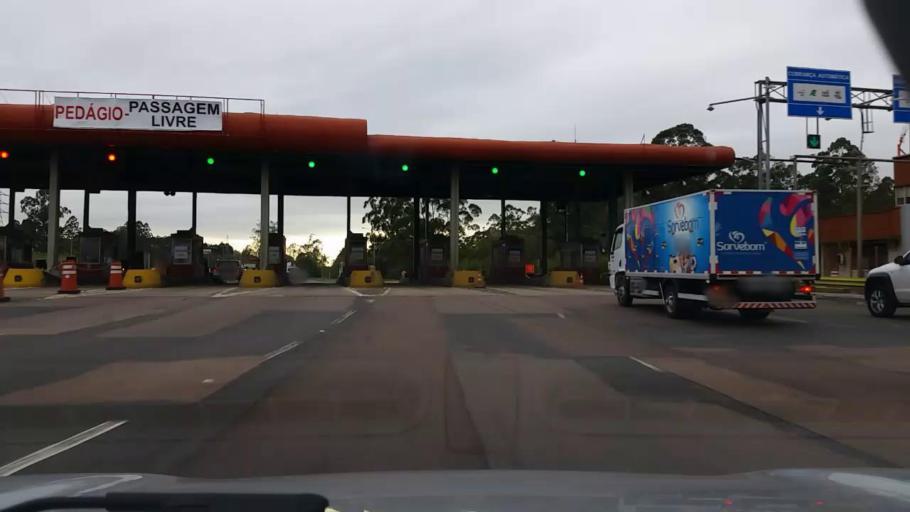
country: BR
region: Rio Grande do Sul
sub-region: Gravatai
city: Gravatai
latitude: -29.9553
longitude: -51.0318
